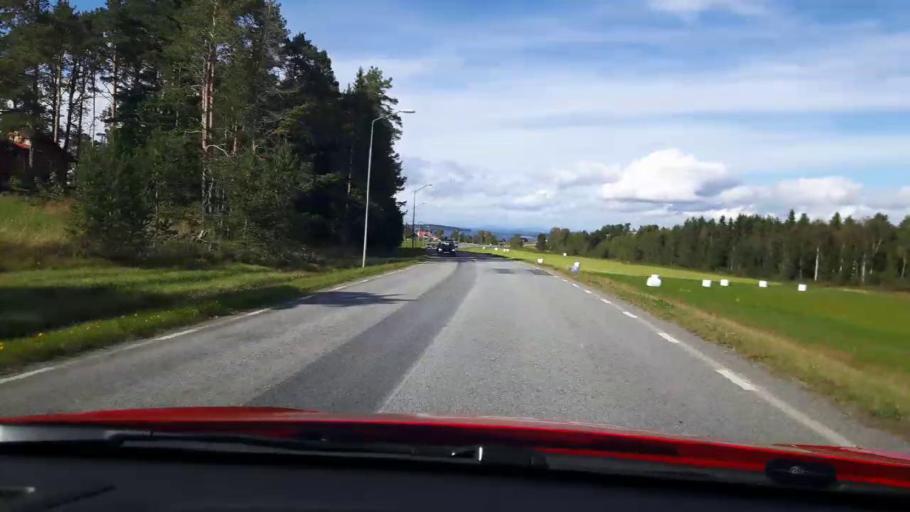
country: SE
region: Jaemtland
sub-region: OEstersunds Kommun
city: Ostersund
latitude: 63.0965
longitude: 14.4384
